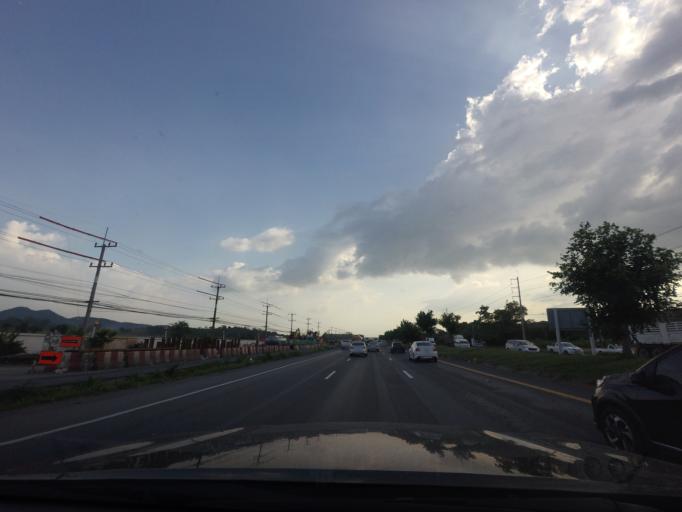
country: TH
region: Sara Buri
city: Saraburi
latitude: 14.4747
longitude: 100.9103
